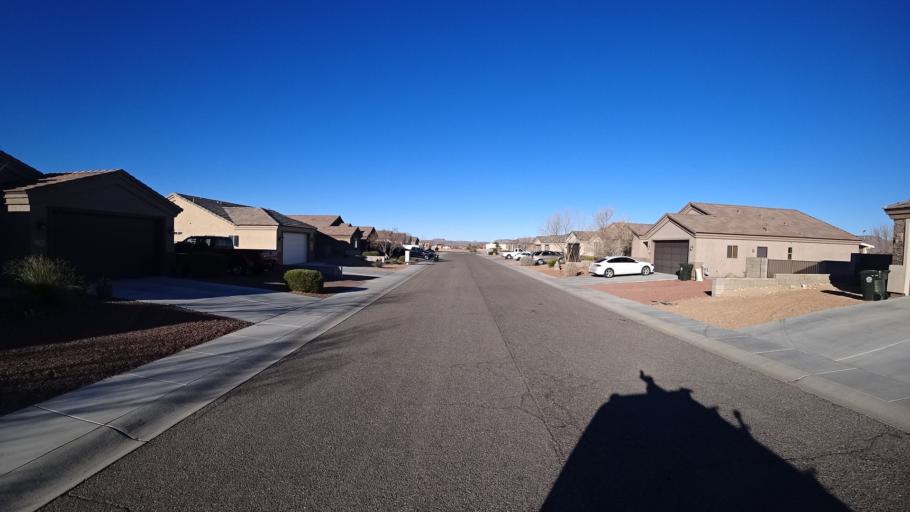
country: US
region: Arizona
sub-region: Mohave County
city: Kingman
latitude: 35.1922
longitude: -114.0013
